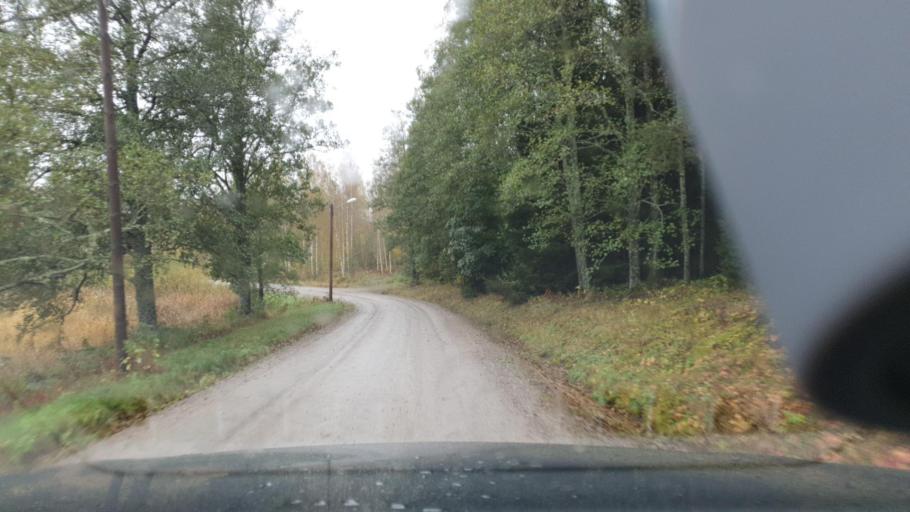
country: SE
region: Vaermland
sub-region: Karlstads Kommun
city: Edsvalla
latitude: 59.6056
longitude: 12.9174
